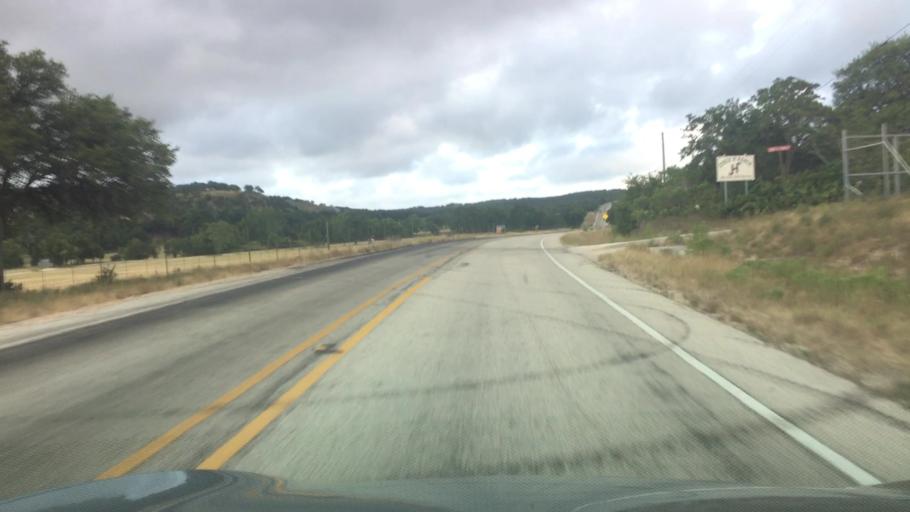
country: US
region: Texas
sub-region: Blanco County
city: Blanco
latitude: 30.1492
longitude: -98.2561
